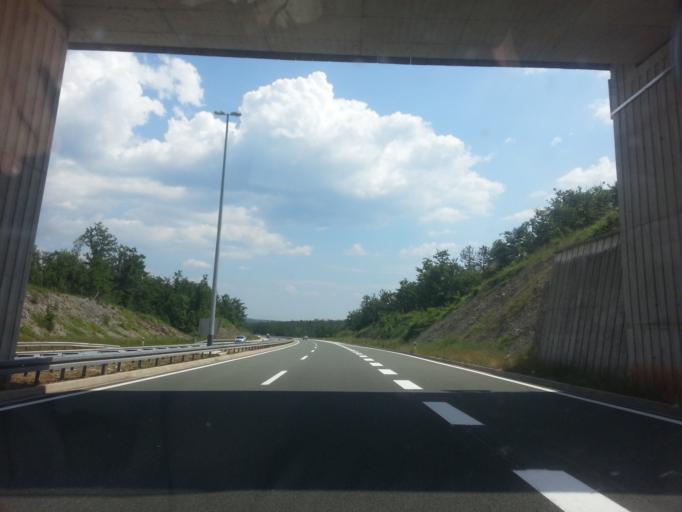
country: HR
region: Primorsko-Goranska
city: Matulji
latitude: 45.4405
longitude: 14.2753
